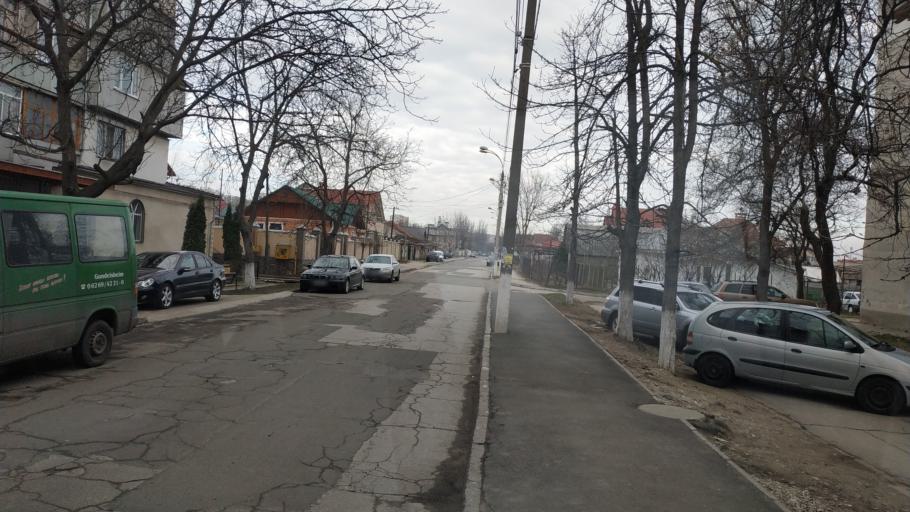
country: MD
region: Chisinau
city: Vatra
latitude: 47.0327
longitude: 28.7869
